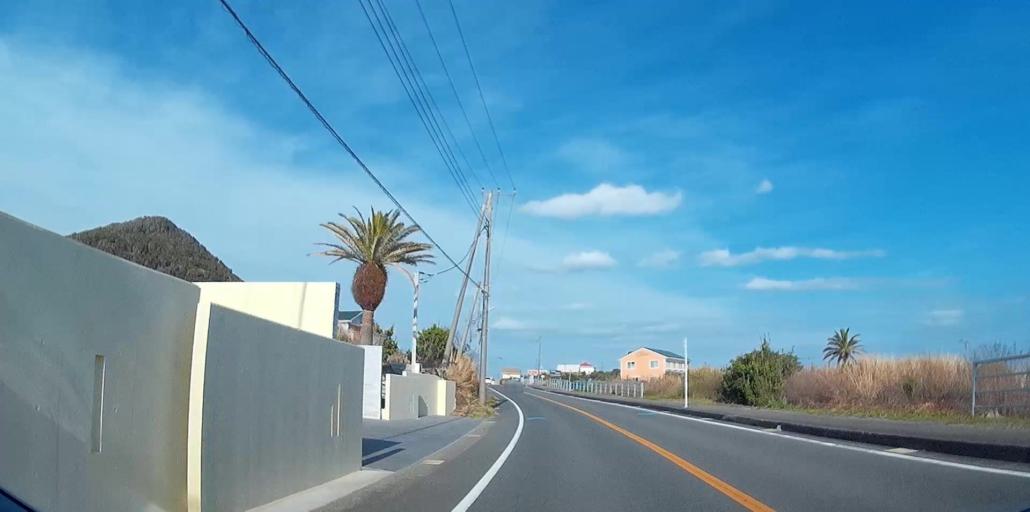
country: JP
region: Chiba
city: Tateyama
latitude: 34.9151
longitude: 139.9334
